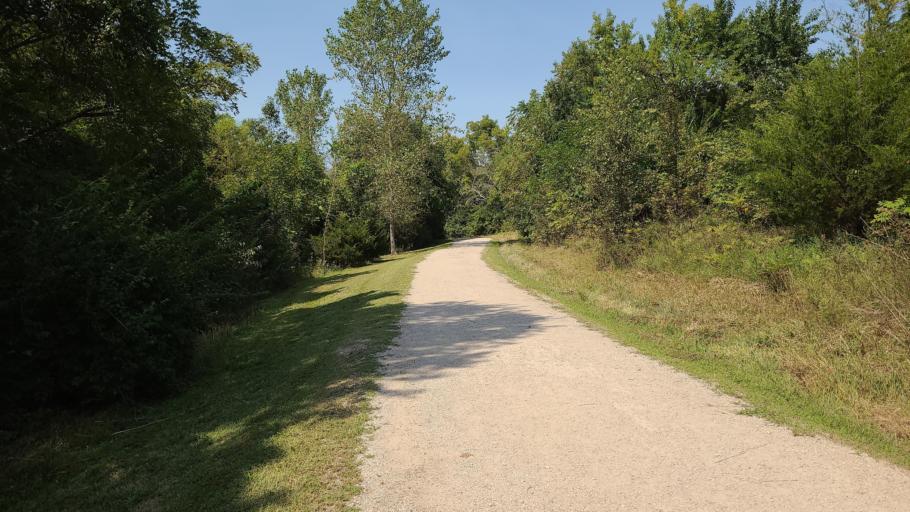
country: US
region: Kansas
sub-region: Douglas County
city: Lawrence
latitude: 38.9579
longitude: -95.3192
